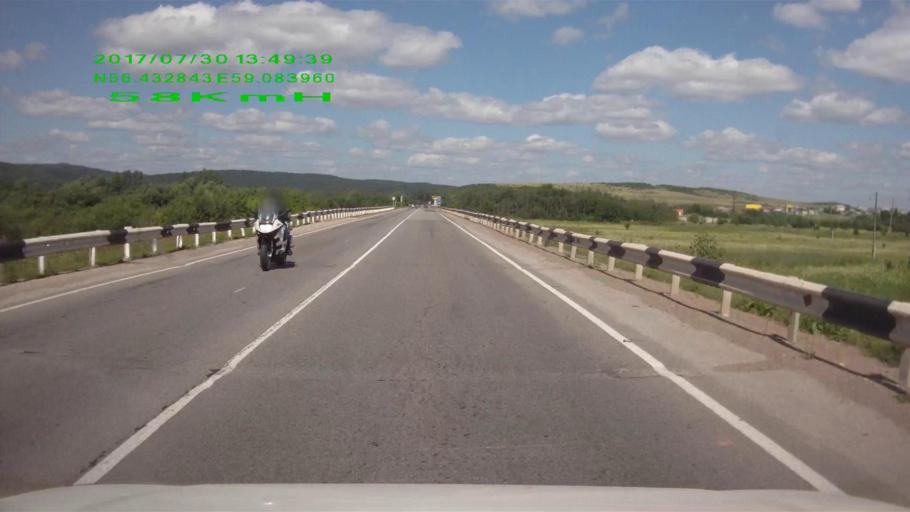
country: RU
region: Sverdlovsk
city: Mikhaylovsk
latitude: 56.4331
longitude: 59.0840
